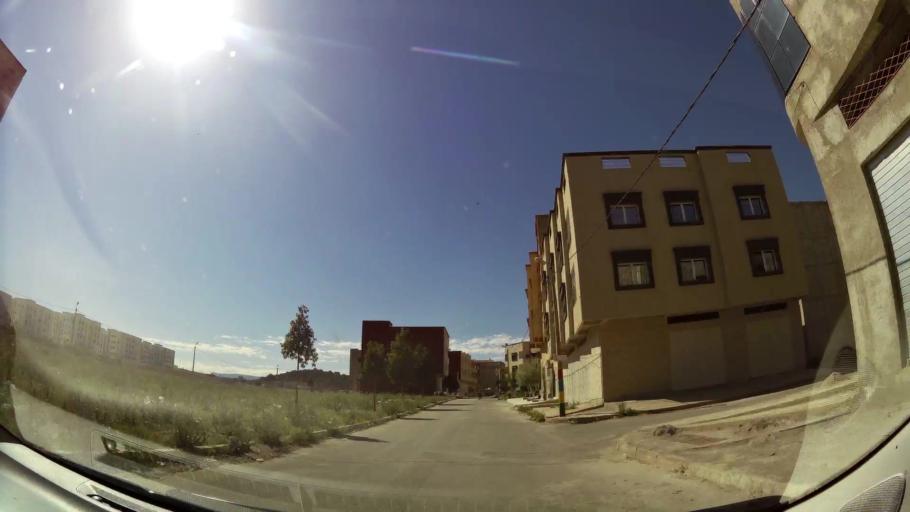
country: MA
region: Oriental
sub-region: Oujda-Angad
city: Oujda
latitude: 34.6518
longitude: -1.8826
